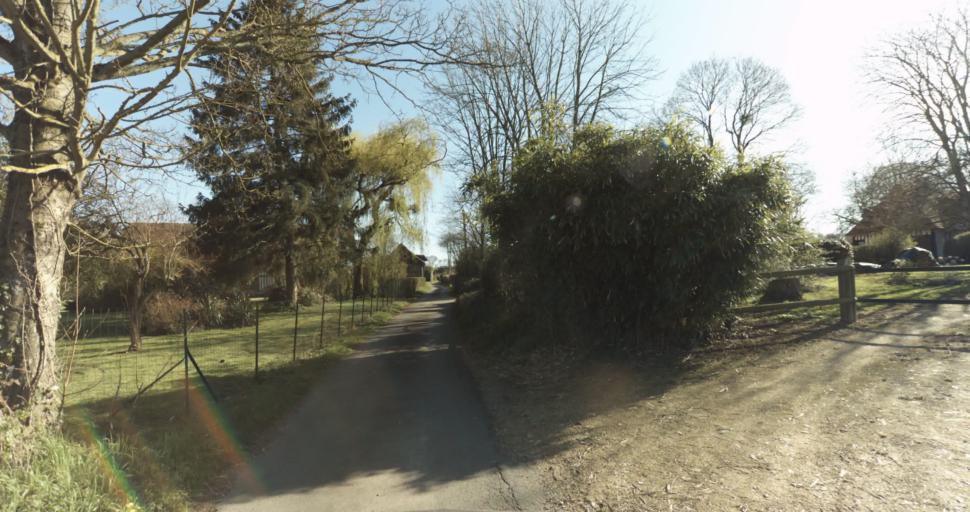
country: FR
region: Lower Normandy
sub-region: Departement du Calvados
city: Saint-Pierre-sur-Dives
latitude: 49.0399
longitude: 0.0577
